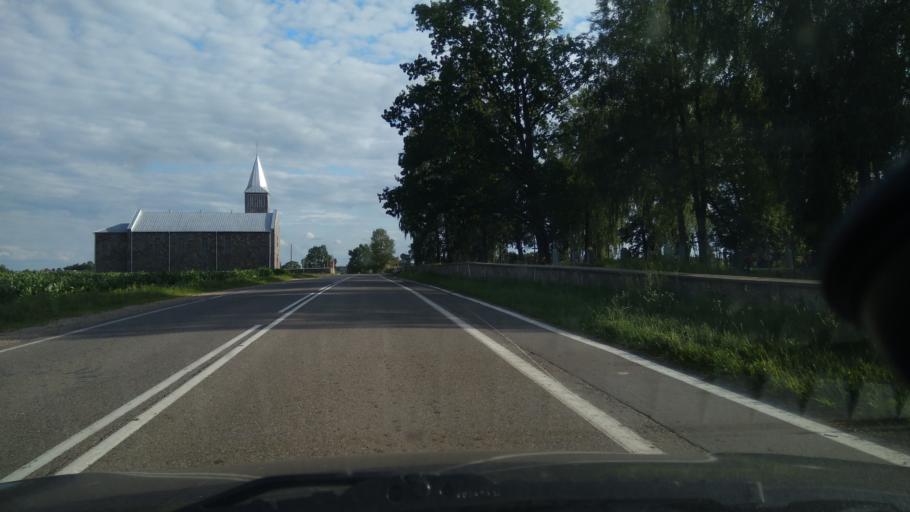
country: BY
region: Grodnenskaya
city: Zel'va
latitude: 53.2762
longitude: 24.6828
